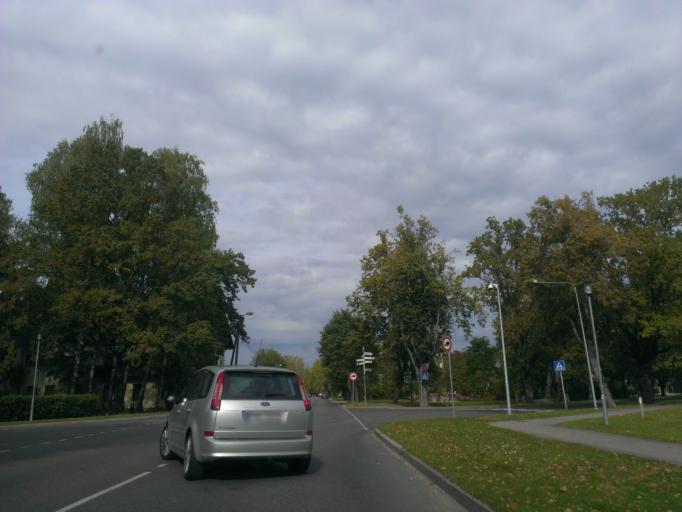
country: LV
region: Sigulda
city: Sigulda
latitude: 57.1589
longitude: 24.8530
